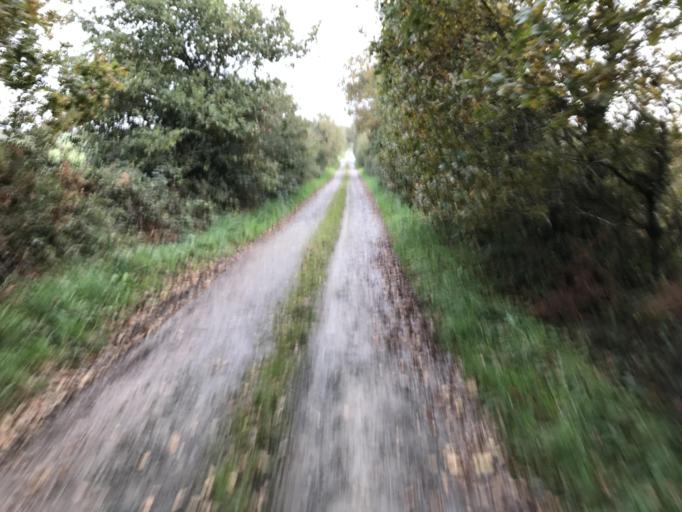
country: FR
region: Brittany
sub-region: Departement du Finistere
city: Hopital-Camfrout
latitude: 48.3330
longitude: -4.2090
